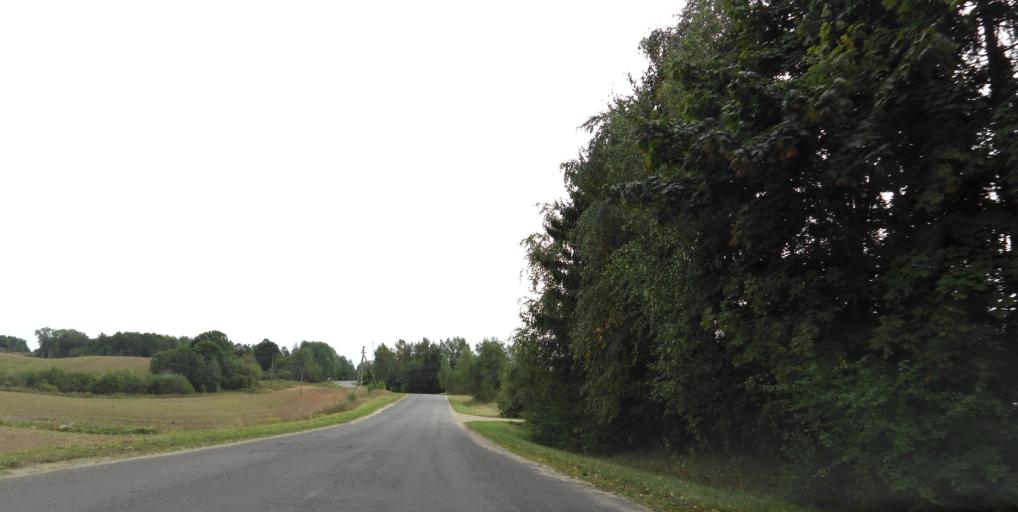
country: LT
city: Grigiskes
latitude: 54.7656
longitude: 25.0347
